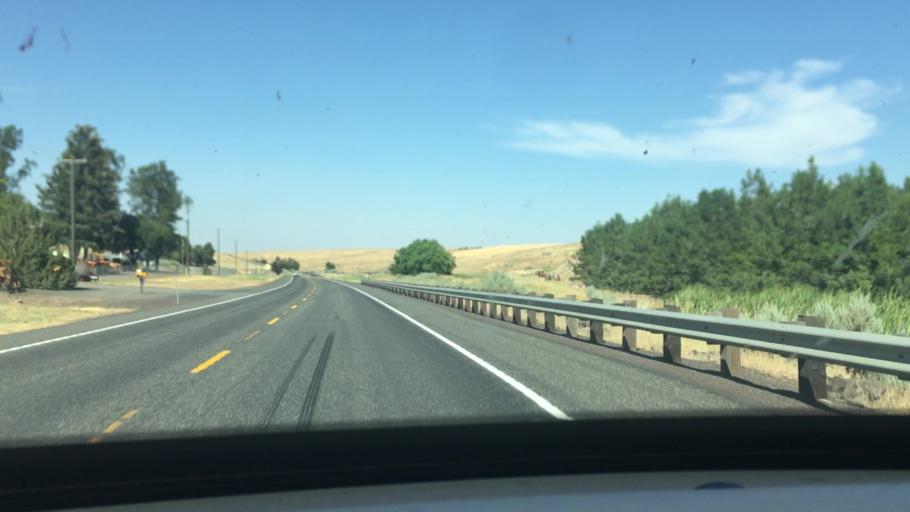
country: US
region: Oregon
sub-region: Sherman County
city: Moro
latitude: 45.4891
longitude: -120.7193
